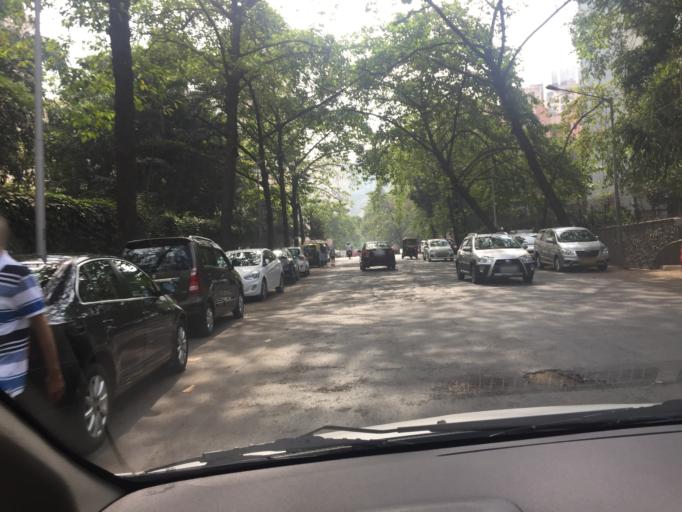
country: IN
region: Maharashtra
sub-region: Mumbai Suburban
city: Powai
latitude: 19.1164
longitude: 72.9080
